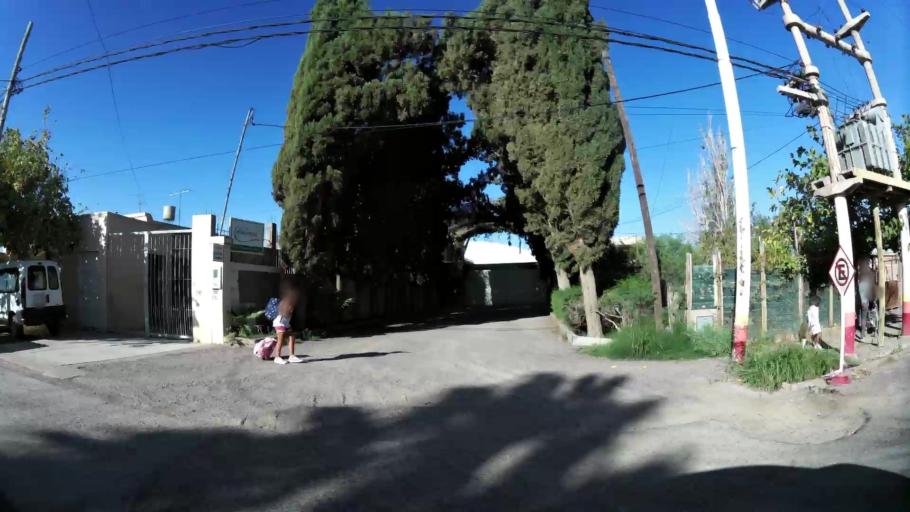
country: AR
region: San Juan
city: Villa Krause
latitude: -31.5666
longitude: -68.5207
